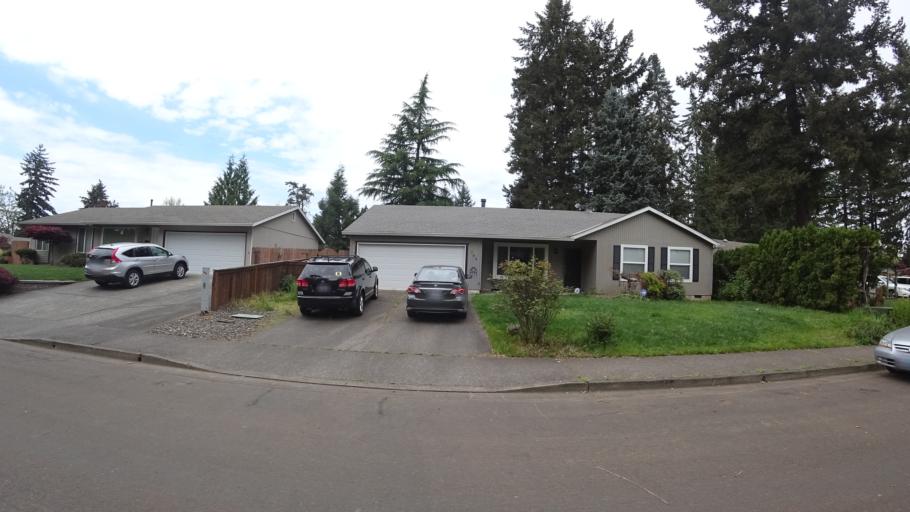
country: US
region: Oregon
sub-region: Washington County
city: Hillsboro
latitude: 45.5145
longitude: -122.9401
